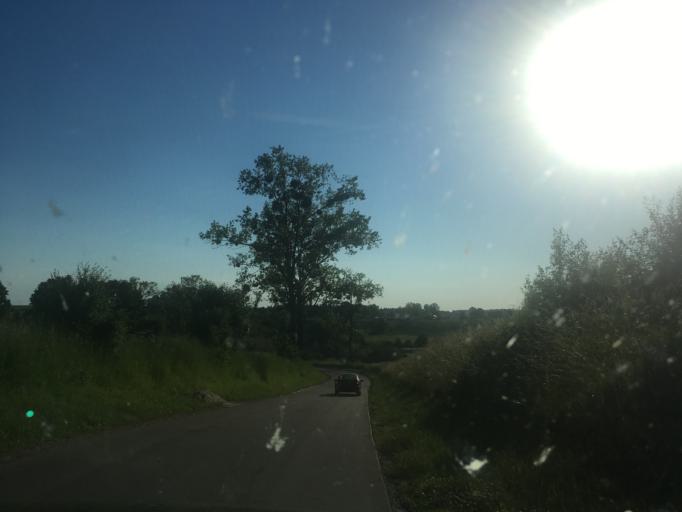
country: PL
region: Warmian-Masurian Voivodeship
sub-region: Powiat ostrodzki
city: Ostroda
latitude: 53.6731
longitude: 20.0374
